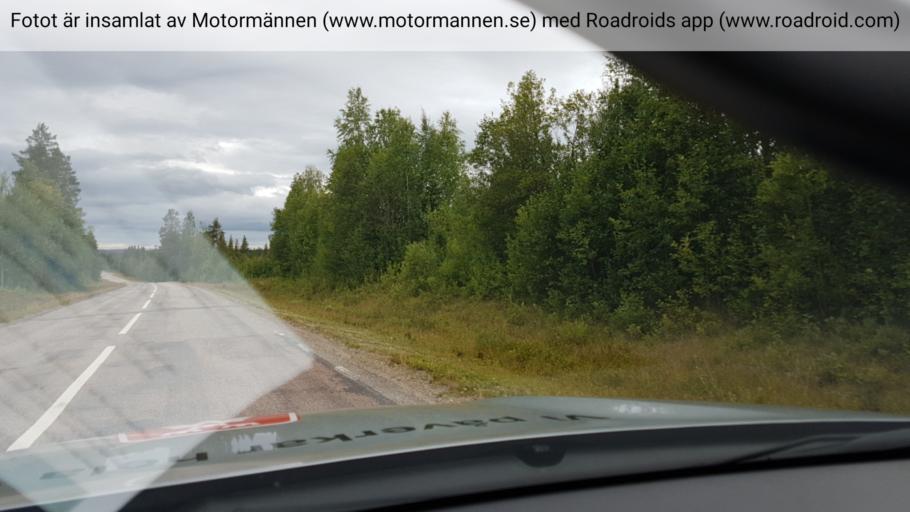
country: SE
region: Norrbotten
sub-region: Overkalix Kommun
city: OEverkalix
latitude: 66.8044
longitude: 22.9651
